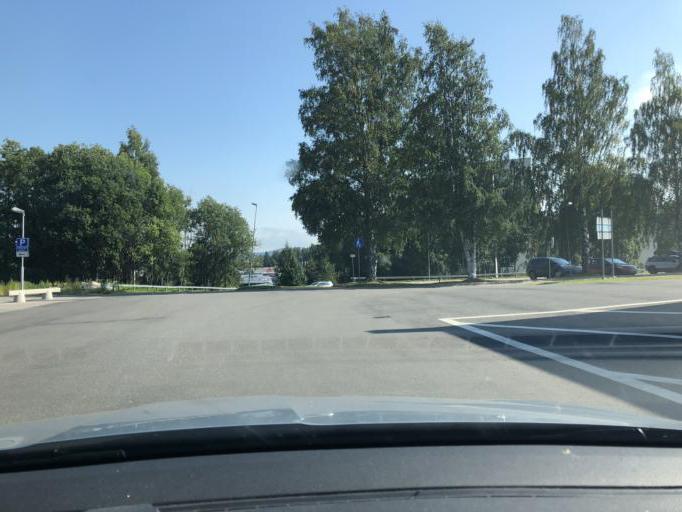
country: SE
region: Vaesternorrland
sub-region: OErnskoeldsviks Kommun
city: Ornskoldsvik
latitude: 63.3013
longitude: 18.7135
